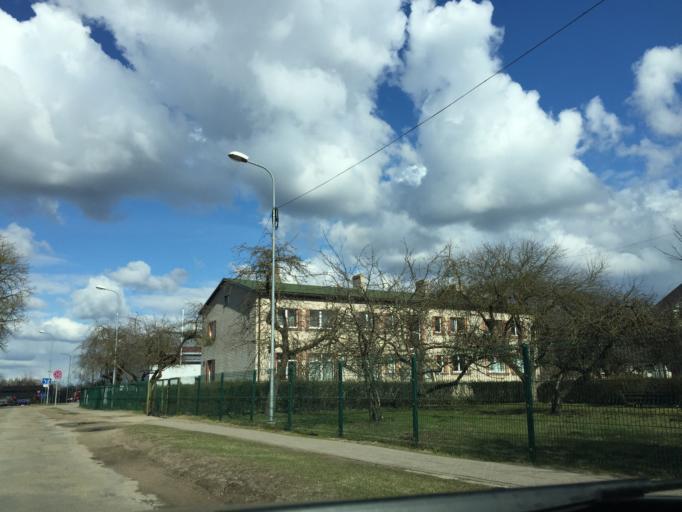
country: LV
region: Kekava
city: Kekava
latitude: 56.8304
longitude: 24.2328
